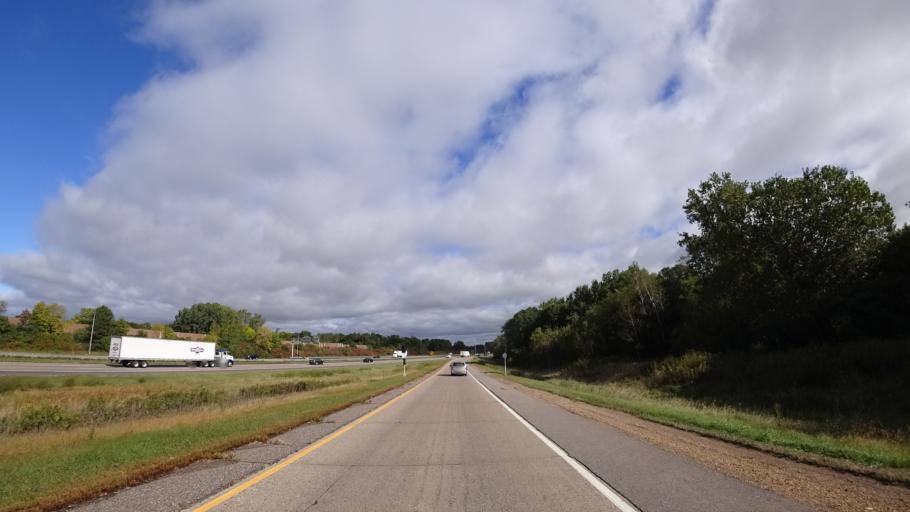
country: US
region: Minnesota
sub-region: Dakota County
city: Eagan
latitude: 44.8062
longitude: -93.1882
